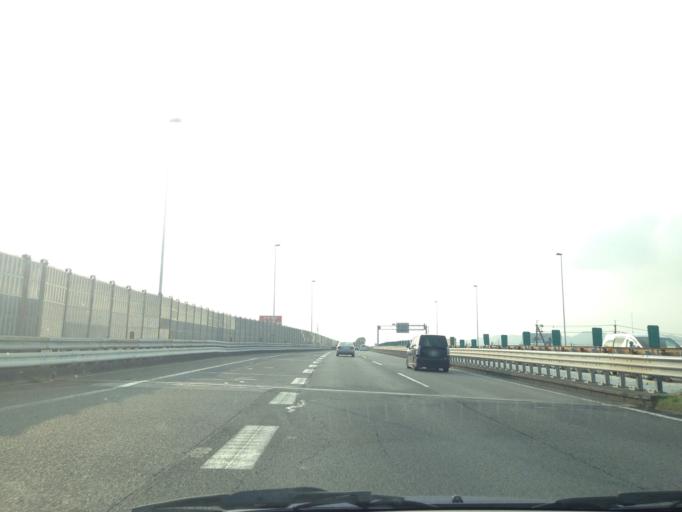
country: JP
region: Aichi
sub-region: Tokai-shi
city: Toyokawa
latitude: 34.8385
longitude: 137.4110
